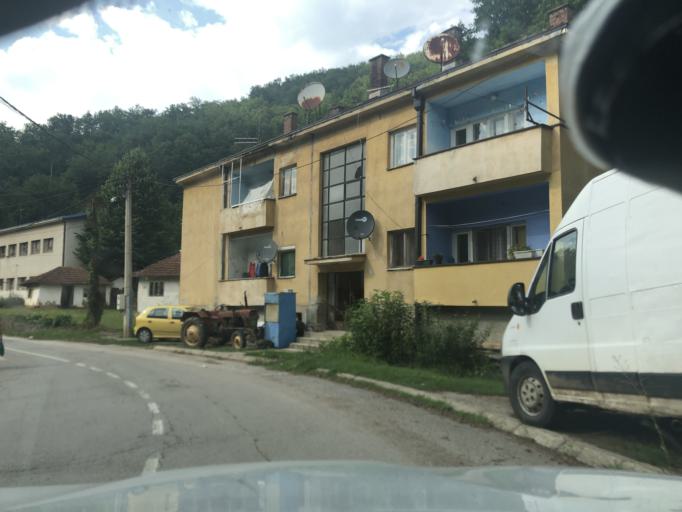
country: RS
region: Central Serbia
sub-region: Jablanicki Okrug
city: Medvega
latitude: 42.7790
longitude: 21.5999
